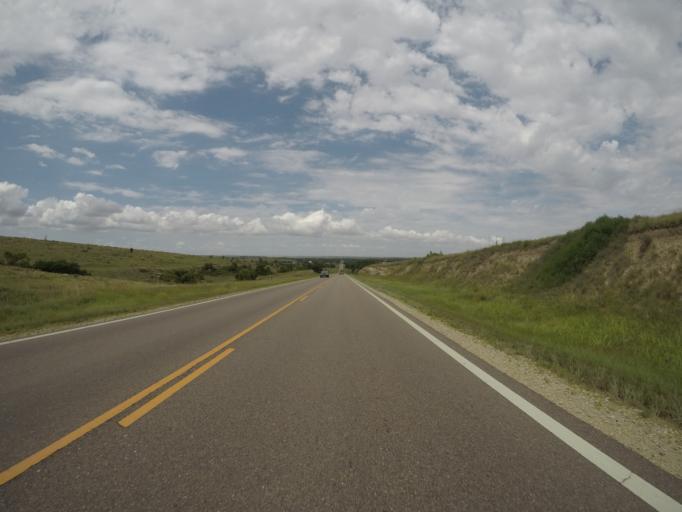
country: US
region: Kansas
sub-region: Rawlins County
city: Atwood
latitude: 39.7879
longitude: -101.0469
